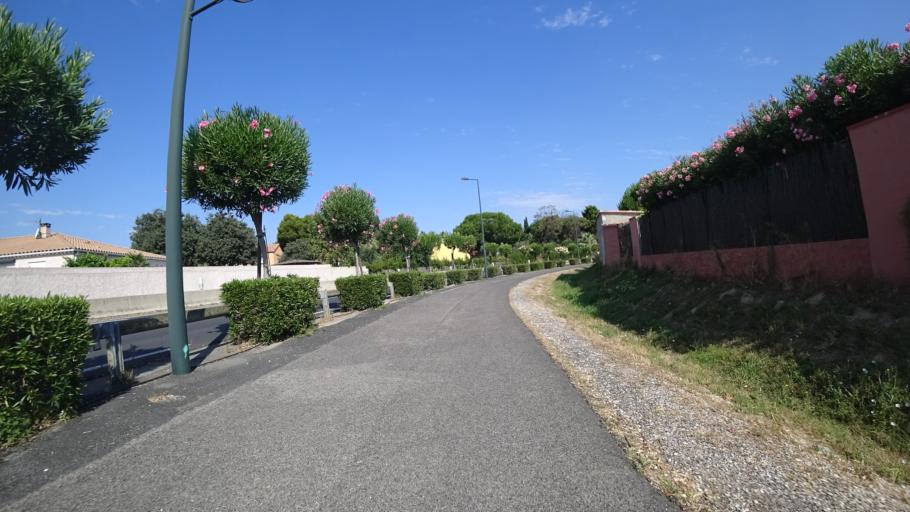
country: FR
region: Languedoc-Roussillon
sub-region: Departement des Pyrenees-Orientales
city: Bompas
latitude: 42.7227
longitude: 2.9266
